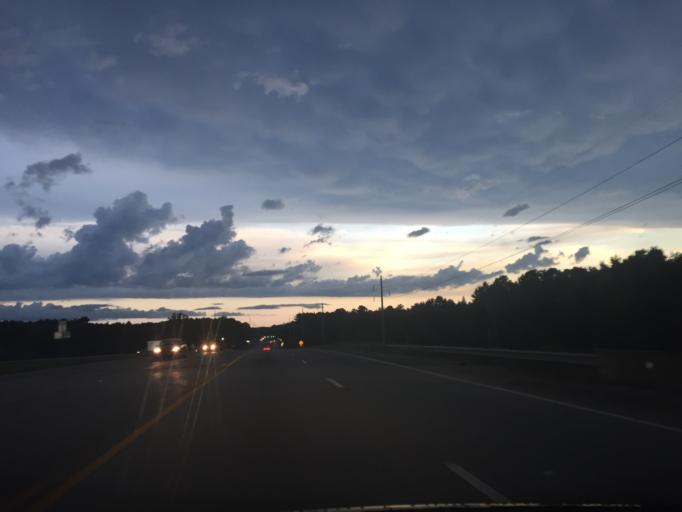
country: US
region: Georgia
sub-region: Liberty County
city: Hinesville
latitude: 31.8275
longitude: -81.5262
